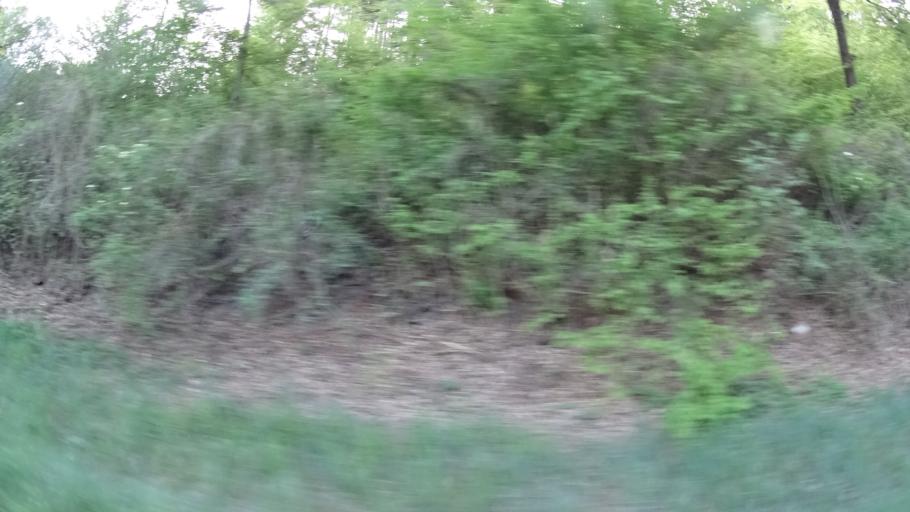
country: DE
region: Baden-Wuerttemberg
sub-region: Tuebingen Region
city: Haigerloch
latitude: 48.3875
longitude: 8.7899
